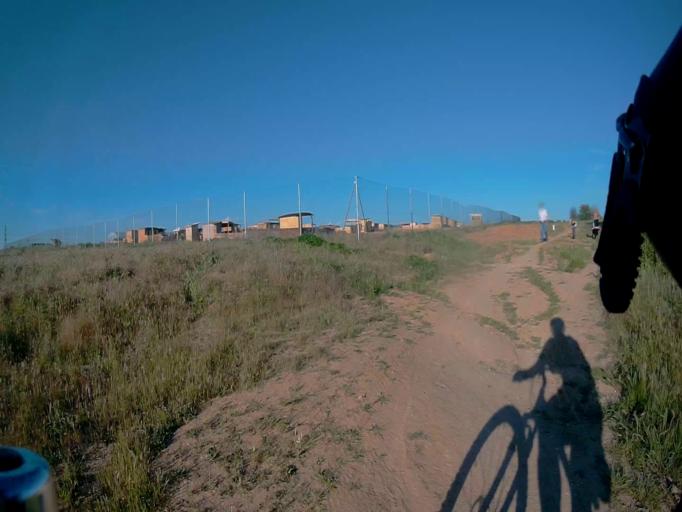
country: ES
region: Madrid
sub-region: Provincia de Madrid
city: Alcorcon
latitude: 40.3210
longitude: -3.8252
